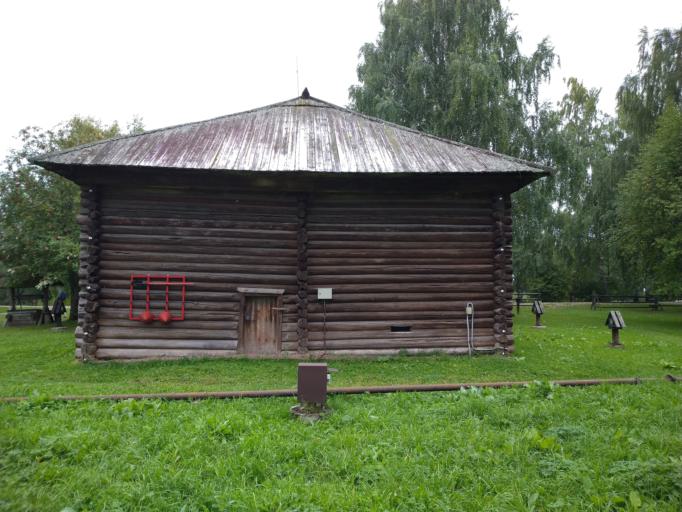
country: RU
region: Kostroma
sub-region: Kostromskoy Rayon
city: Kostroma
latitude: 57.7753
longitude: 40.8933
